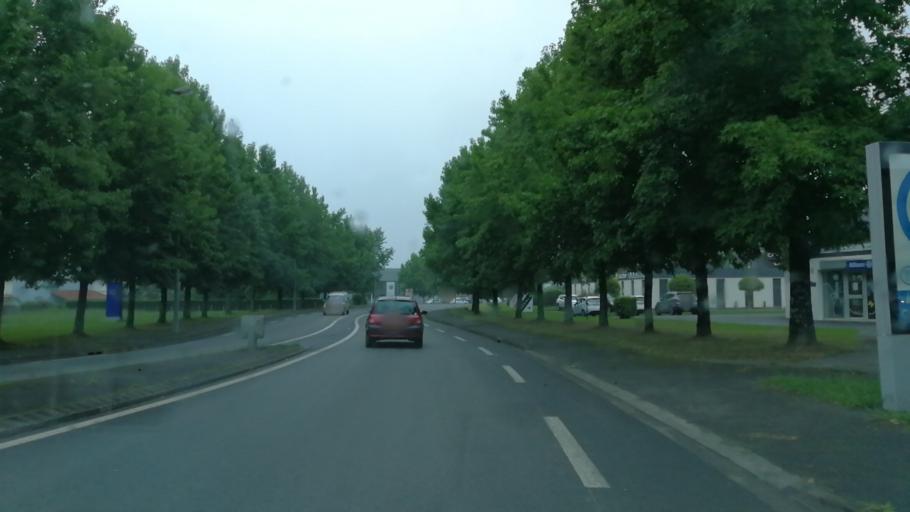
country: FR
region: Aquitaine
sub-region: Departement des Pyrenees-Atlantiques
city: Oloron-Sainte-Marie
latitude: 43.1873
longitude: -0.6250
